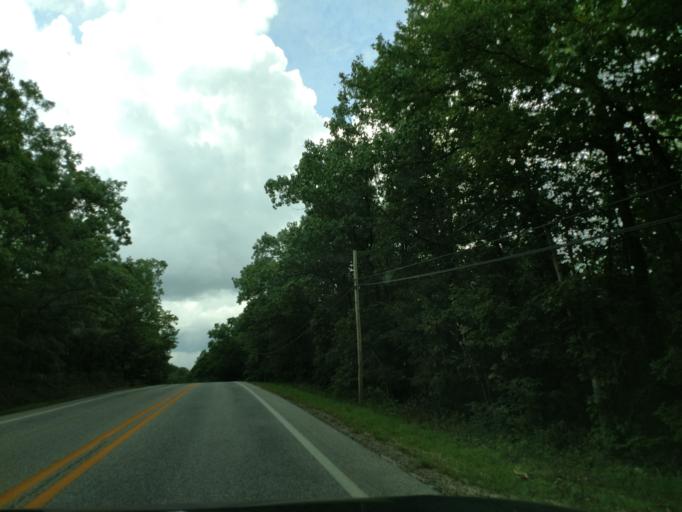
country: US
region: Arkansas
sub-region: Boone County
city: Harrison
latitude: 36.2405
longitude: -93.2118
